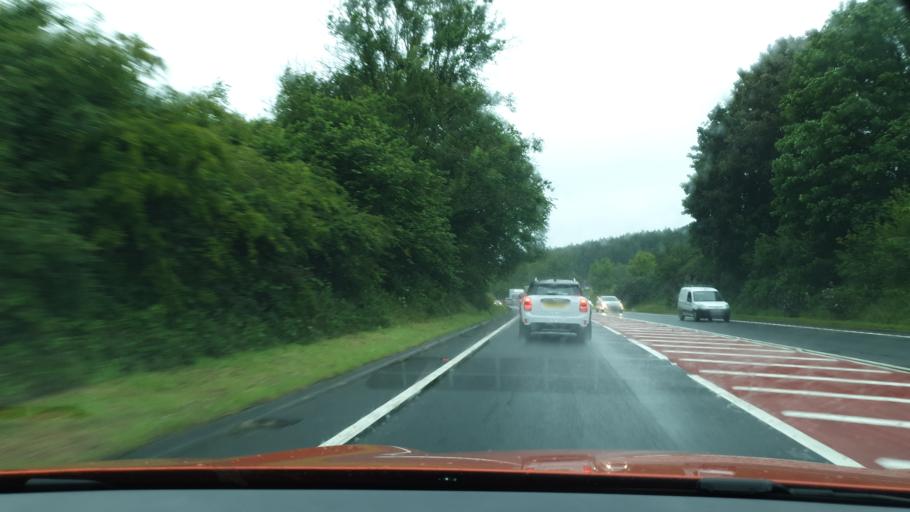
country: GB
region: England
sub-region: Cumbria
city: Grange-over-Sands
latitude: 54.2542
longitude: -2.9434
